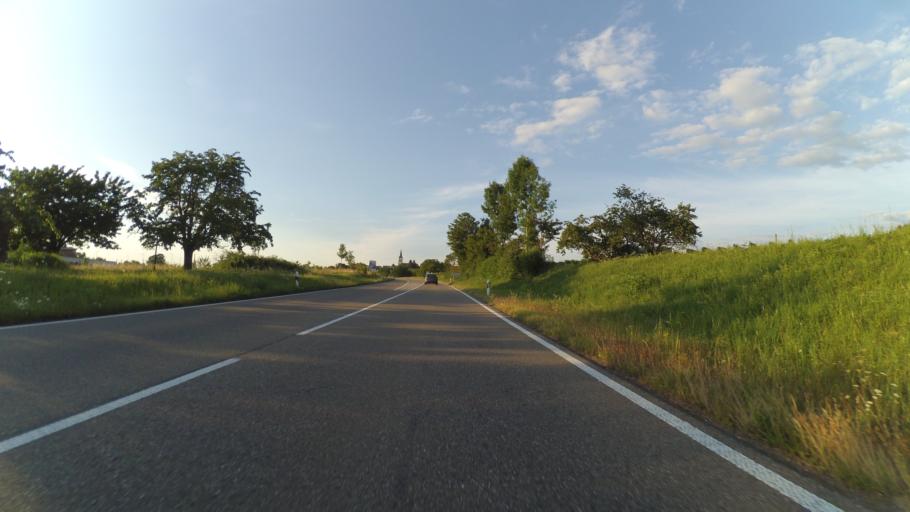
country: DE
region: Baden-Wuerttemberg
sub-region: Freiburg Region
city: Sulzburg
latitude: 47.8526
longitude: 7.6978
